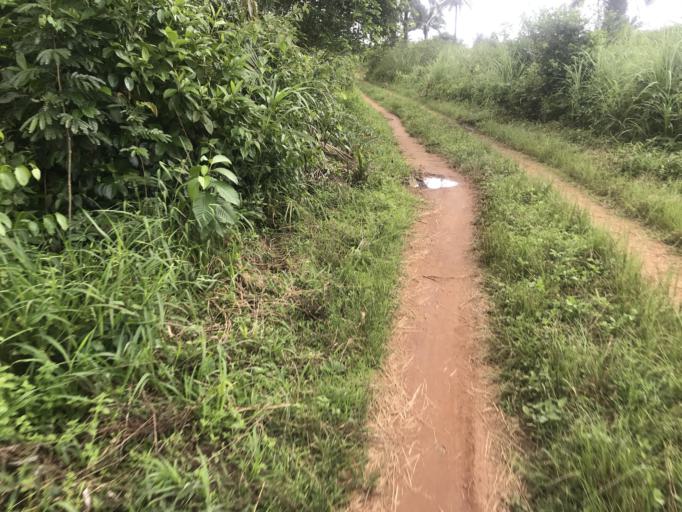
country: GN
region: Nzerekore
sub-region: Prefecture de Guekedou
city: Gueckedou
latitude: 8.4789
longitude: -10.2952
